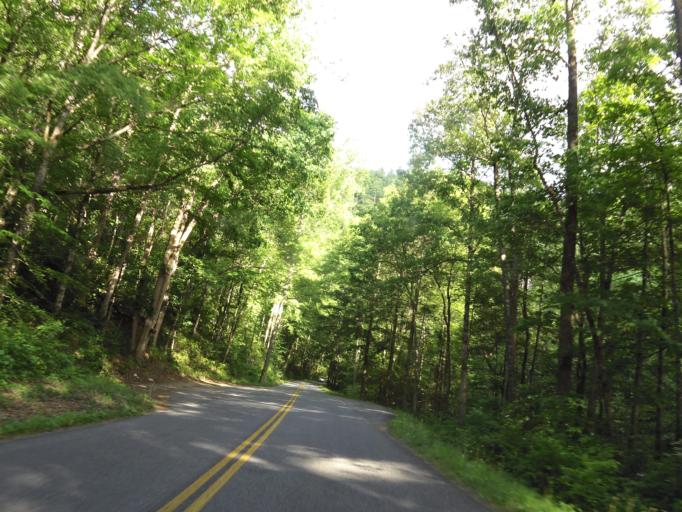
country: US
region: Tennessee
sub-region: Sevier County
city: Pigeon Forge
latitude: 35.6685
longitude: -83.6834
